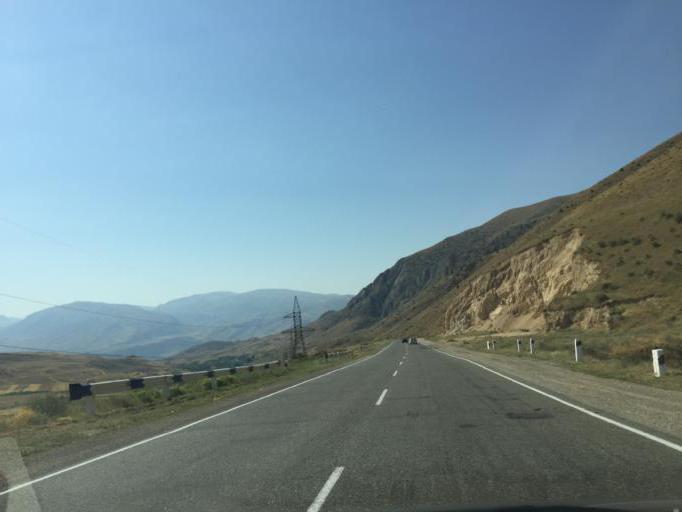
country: AM
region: Vayots' Dzori Marz
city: Rrind
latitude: 39.7892
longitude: 45.1110
